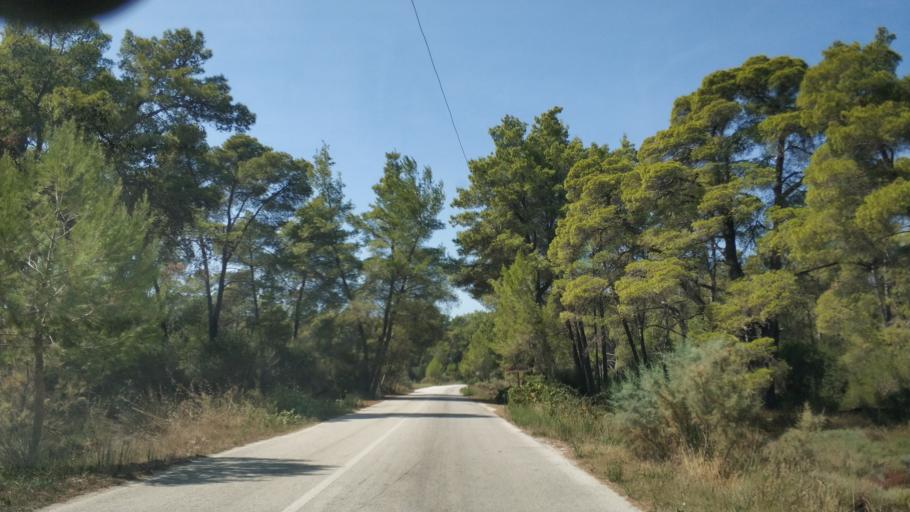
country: AL
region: Fier
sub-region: Rrethi i Lushnjes
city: Divjake
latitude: 40.9901
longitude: 19.4957
